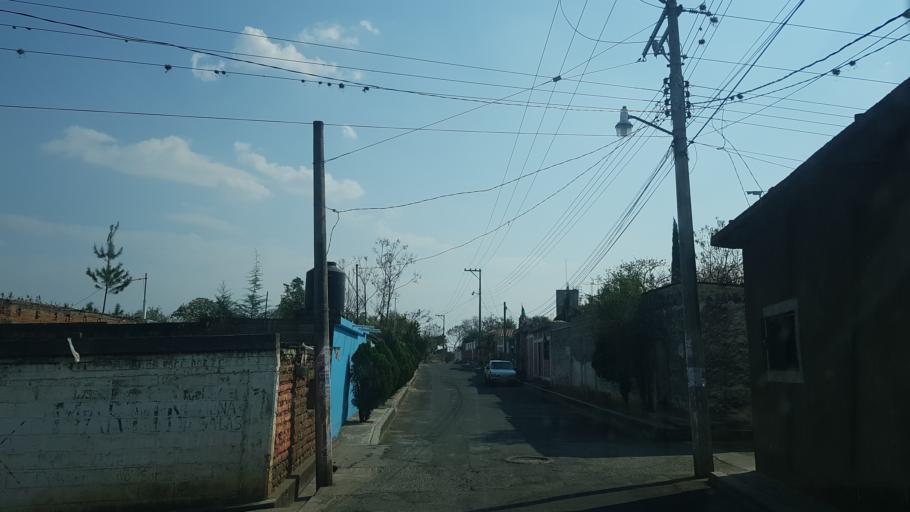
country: MX
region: Morelos
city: Tlacotepec
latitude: 18.8094
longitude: -98.7127
